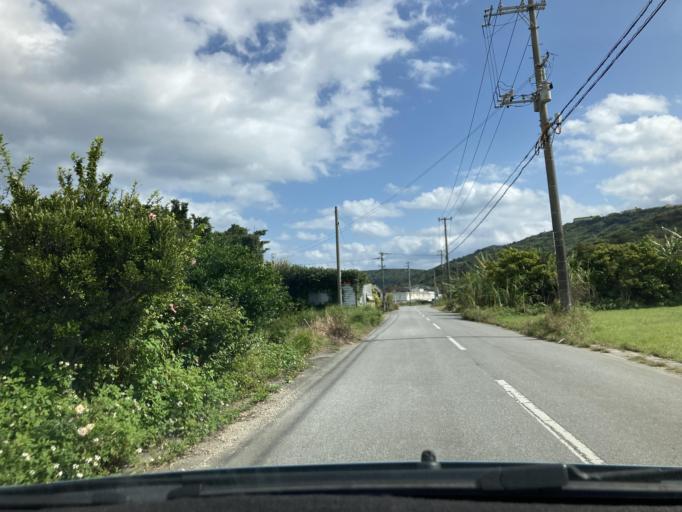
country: JP
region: Okinawa
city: Ginowan
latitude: 26.1688
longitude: 127.7795
